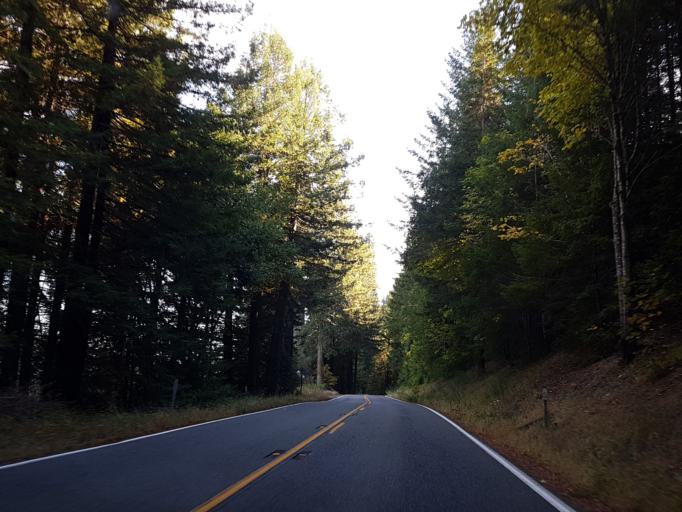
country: US
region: California
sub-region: Humboldt County
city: Rio Dell
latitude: 40.4296
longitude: -123.9838
